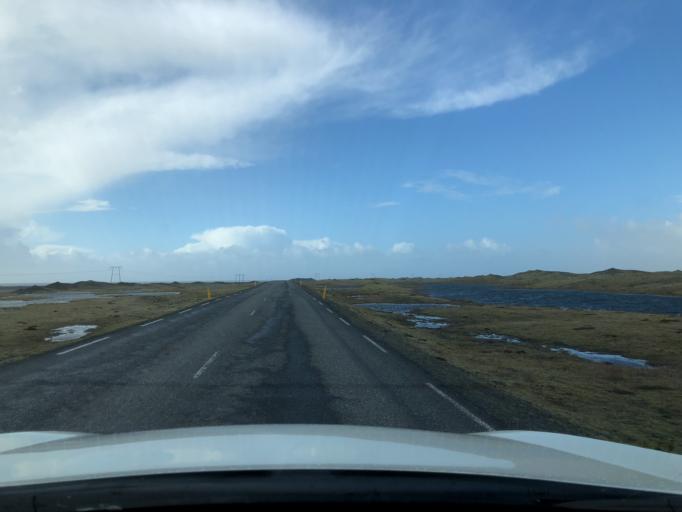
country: IS
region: East
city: Hoefn
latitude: 64.0827
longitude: -16.1070
